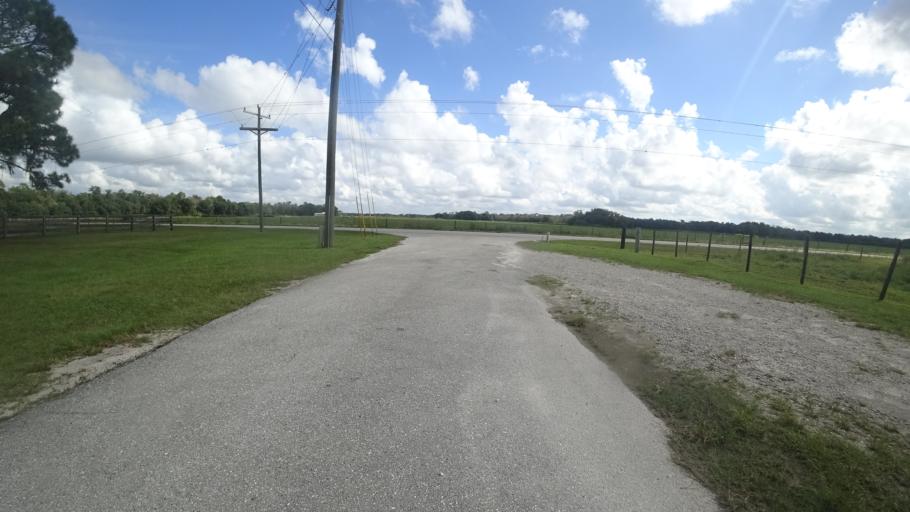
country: US
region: Florida
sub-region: Hillsborough County
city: Wimauma
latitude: 27.5518
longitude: -82.1042
